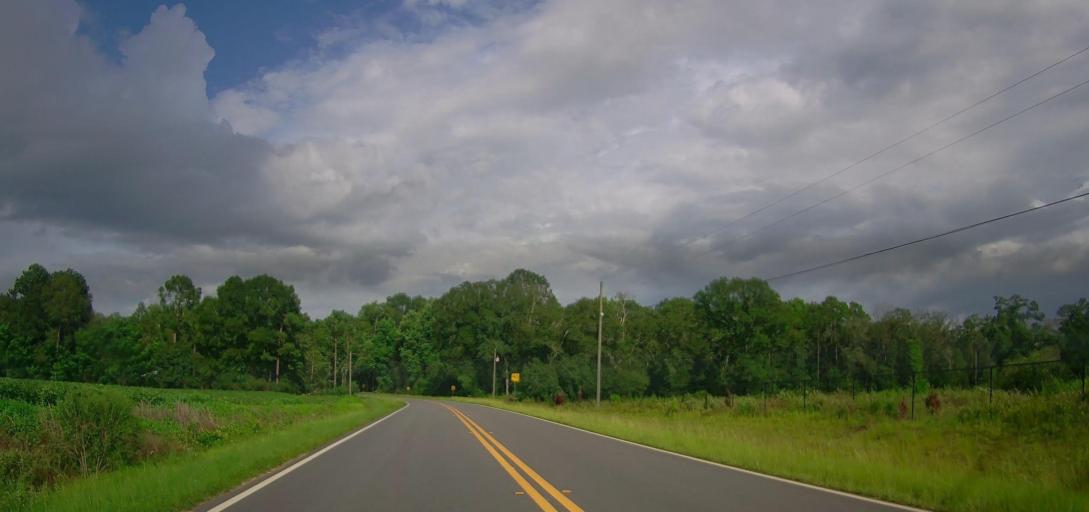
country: US
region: Georgia
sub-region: Coffee County
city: Douglas
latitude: 31.4484
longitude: -82.8704
